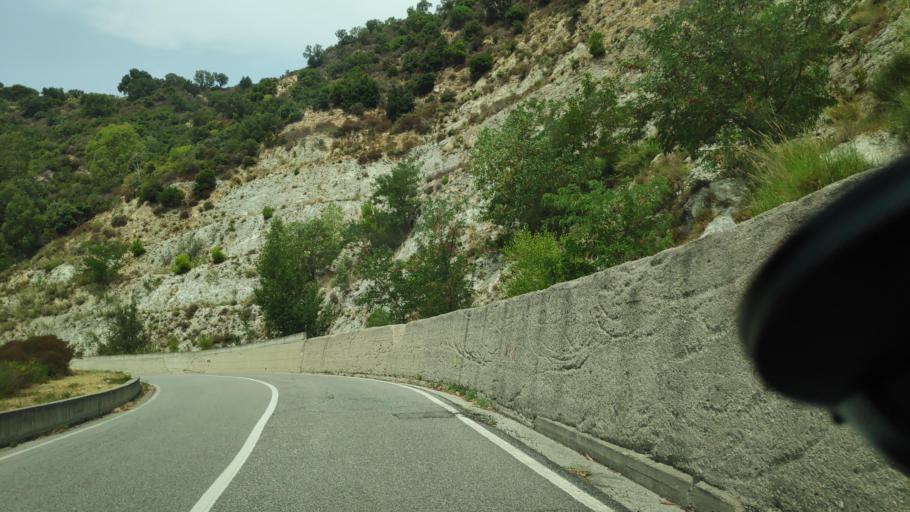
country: IT
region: Calabria
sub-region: Provincia di Catanzaro
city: San Sostene
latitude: 38.6426
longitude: 16.5137
